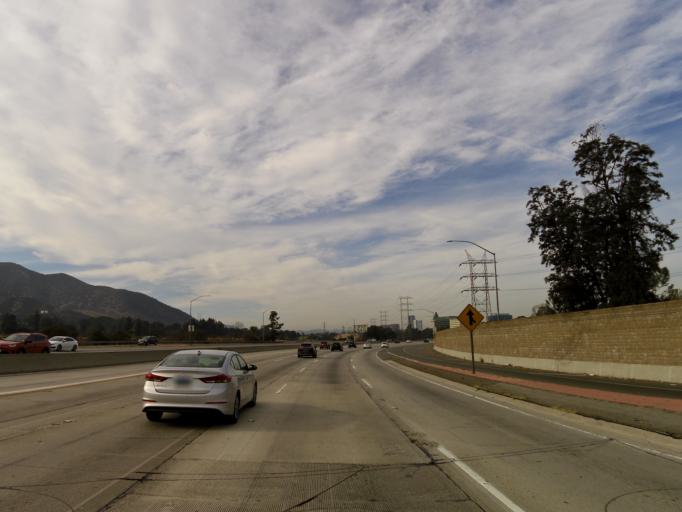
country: US
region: California
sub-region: Los Angeles County
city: Burbank
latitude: 34.1547
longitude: -118.3123
